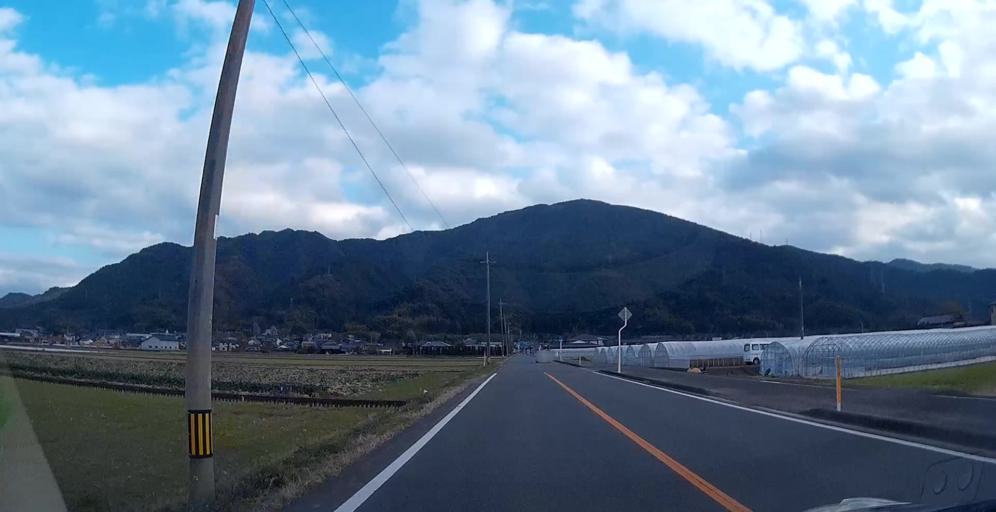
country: JP
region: Kumamoto
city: Yatsushiro
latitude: 32.5299
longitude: 130.6567
